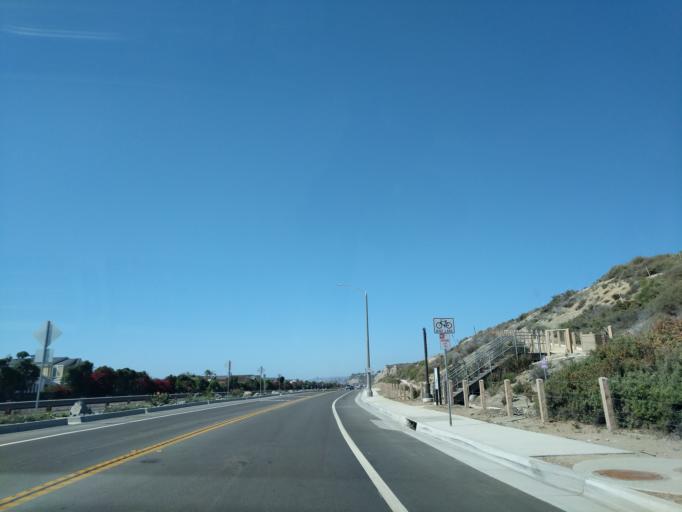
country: US
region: California
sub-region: Orange County
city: San Clemente
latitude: 33.4333
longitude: -117.6341
